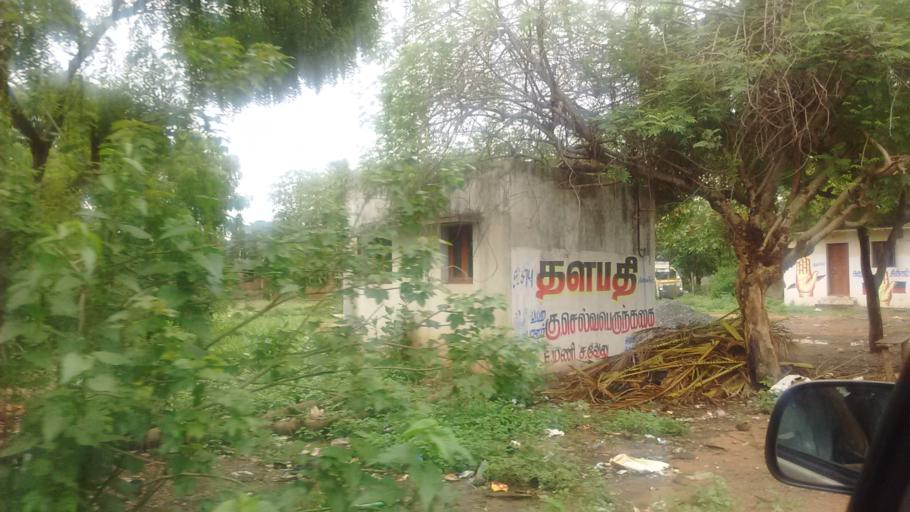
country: IN
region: Tamil Nadu
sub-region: Kancheepuram
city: Madambakkam
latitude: 12.8906
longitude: 80.0118
